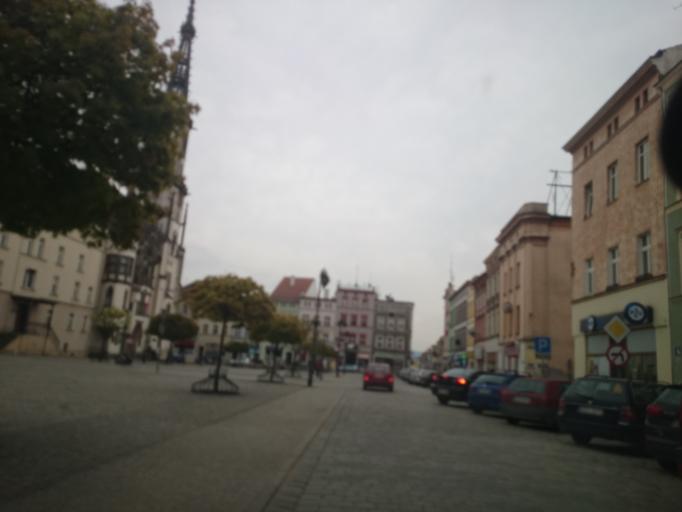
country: PL
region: Lower Silesian Voivodeship
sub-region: Powiat zabkowicki
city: Zabkowice Slaskie
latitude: 50.5898
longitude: 16.8112
